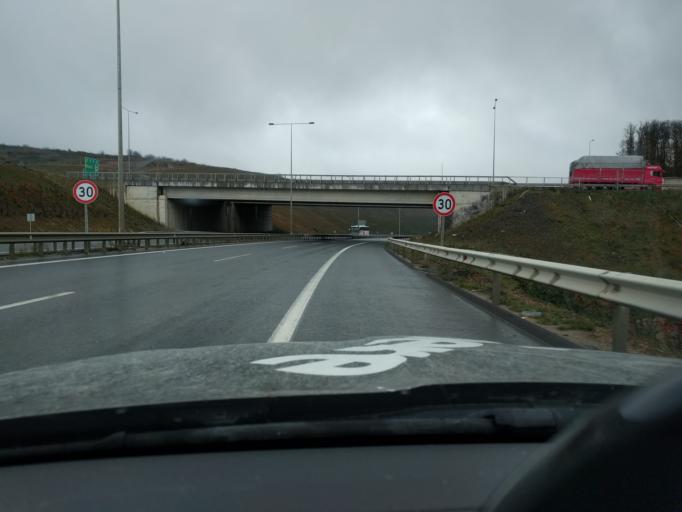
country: TR
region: Istanbul
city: Kemerburgaz
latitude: 41.2111
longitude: 28.8275
